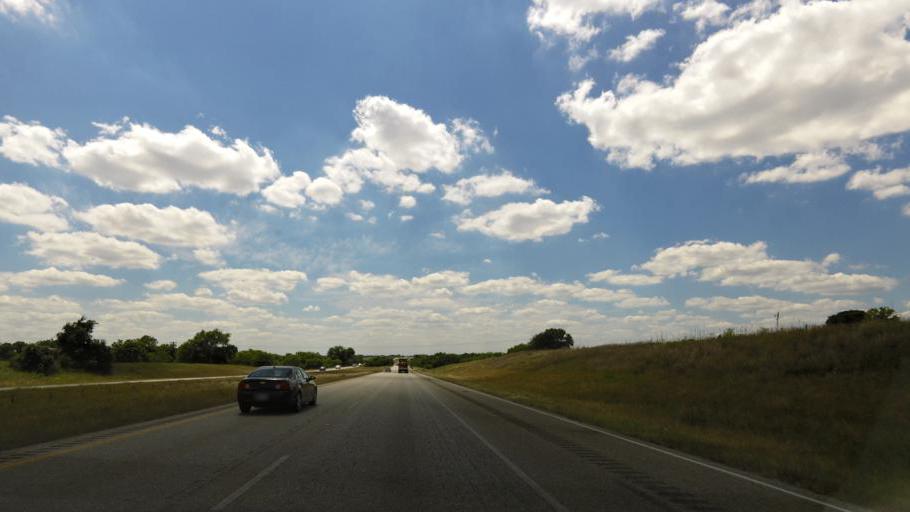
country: US
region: Texas
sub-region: Fayette County
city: Schulenburg
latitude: 29.6901
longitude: -96.9344
